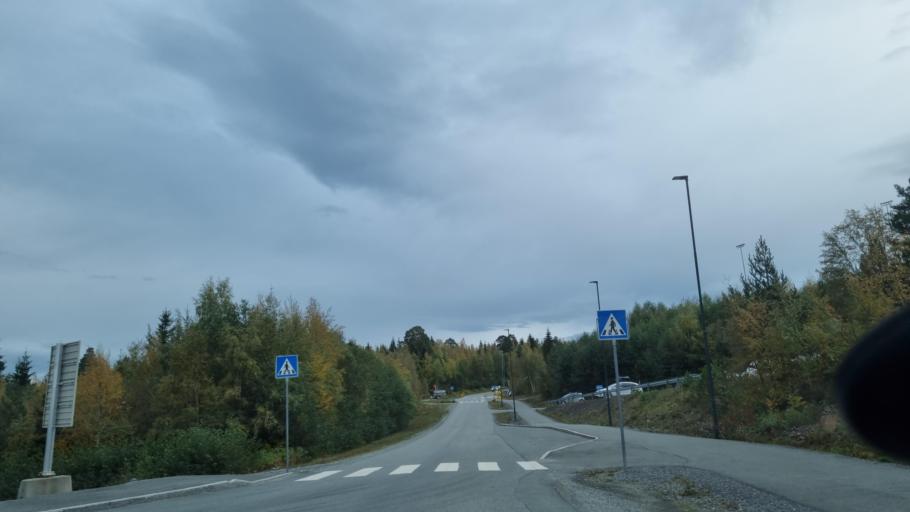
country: NO
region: Sor-Trondelag
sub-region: Malvik
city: Hommelvik
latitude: 63.4243
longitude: 10.7627
